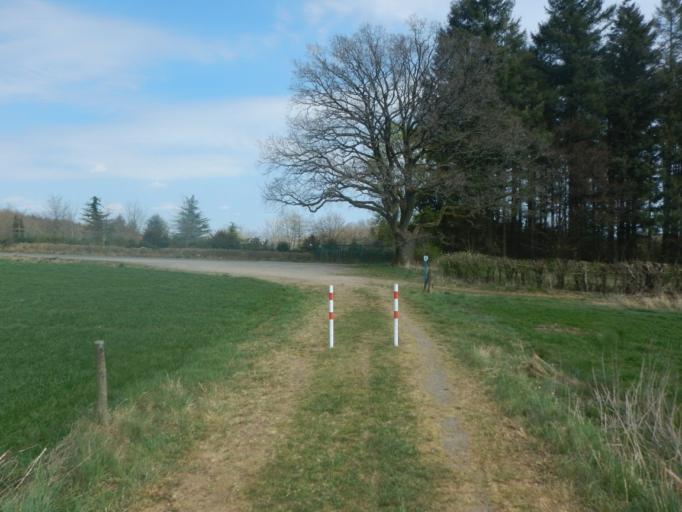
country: LU
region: Diekirch
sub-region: Canton de Clervaux
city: Clervaux
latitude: 50.0557
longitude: 6.0168
